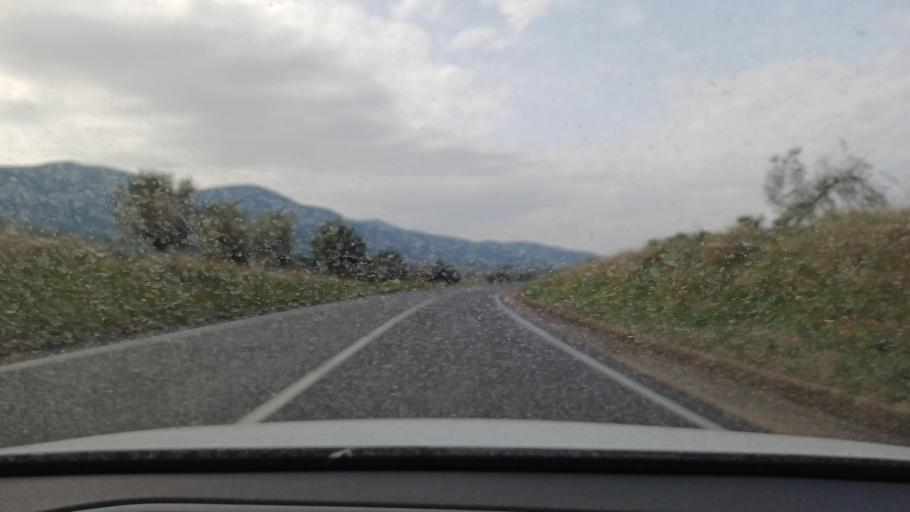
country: ES
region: Catalonia
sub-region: Provincia de Tarragona
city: Masdenverge
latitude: 40.6742
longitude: 0.5265
